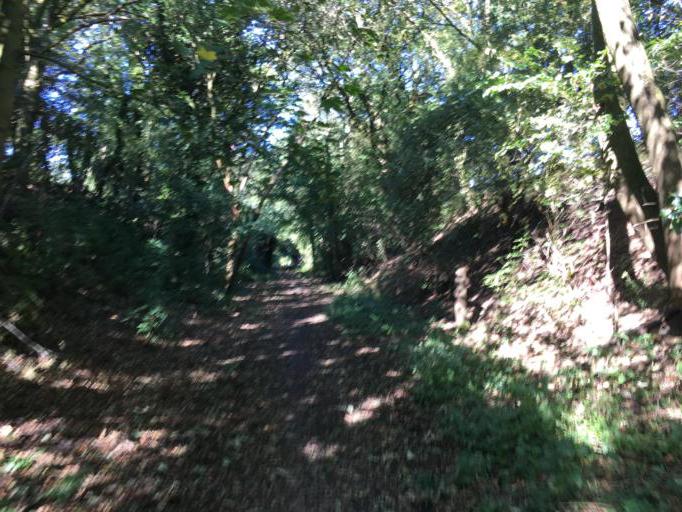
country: GB
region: England
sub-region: Solihull
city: Balsall Common
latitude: 52.3869
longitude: -1.6200
